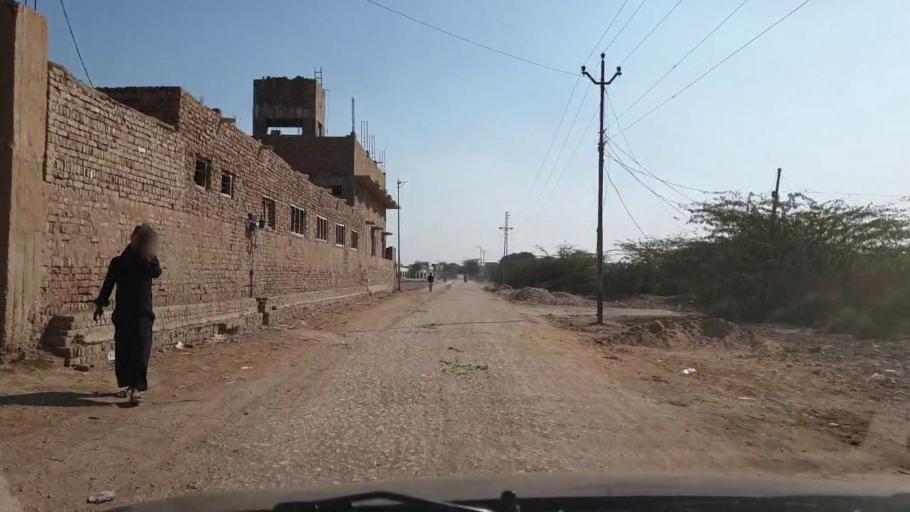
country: PK
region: Sindh
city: Jhol
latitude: 25.9533
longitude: 68.8856
